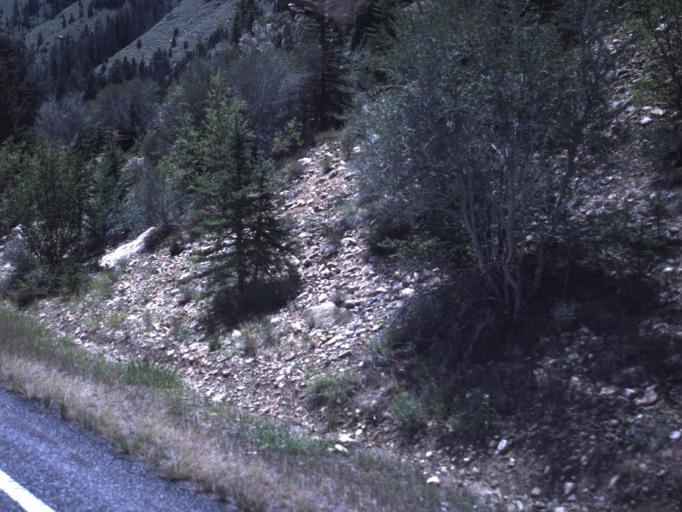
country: US
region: Utah
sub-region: Emery County
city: Huntington
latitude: 39.4813
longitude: -111.1580
